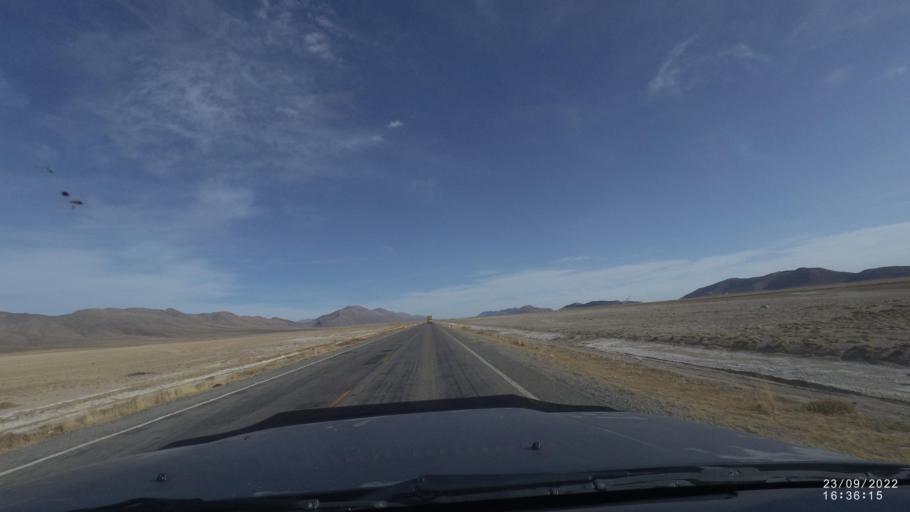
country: BO
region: Oruro
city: Machacamarca
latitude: -18.2168
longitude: -67.0085
